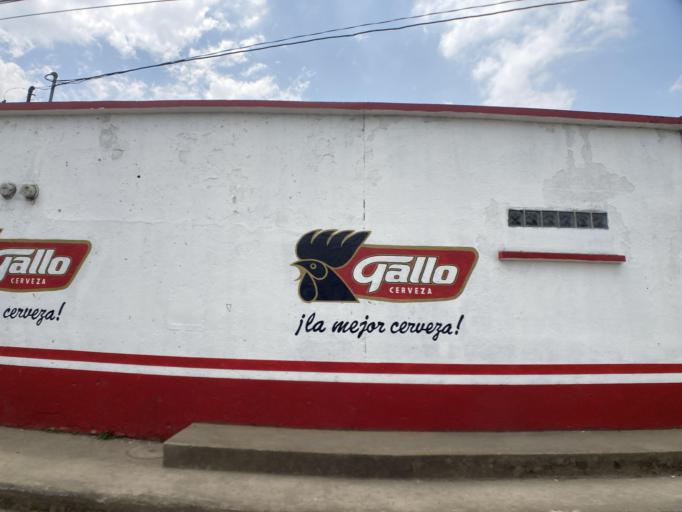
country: GT
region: Guatemala
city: Villa Canales
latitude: 14.4042
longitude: -90.5459
